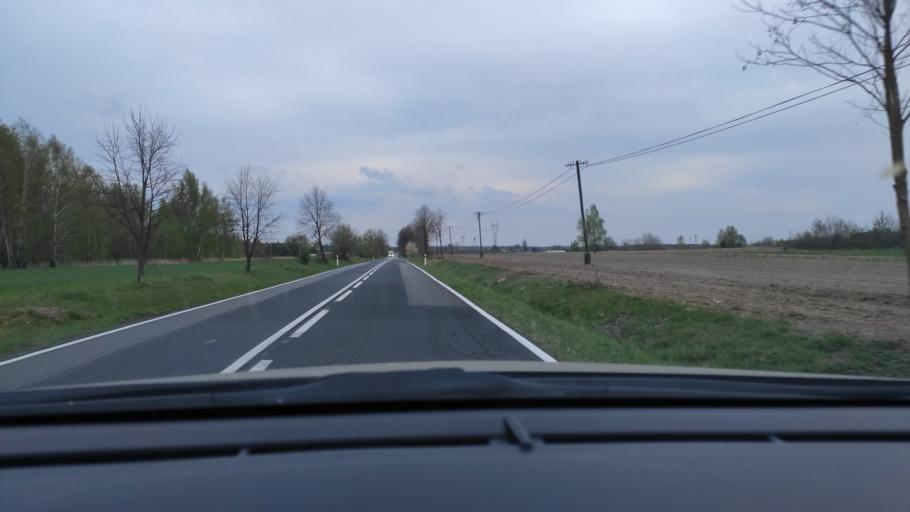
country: PL
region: Masovian Voivodeship
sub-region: Powiat zwolenski
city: Zwolen
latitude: 51.3711
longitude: 21.5635
